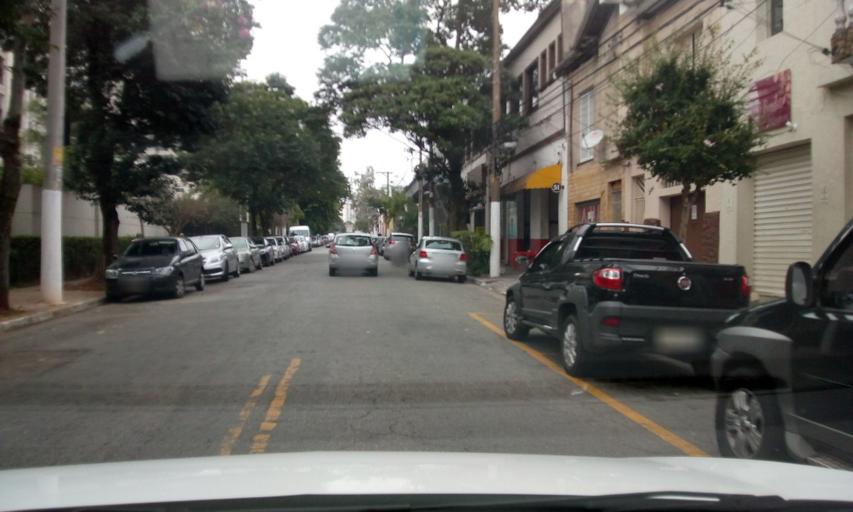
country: BR
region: Sao Paulo
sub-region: Sao Paulo
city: Sao Paulo
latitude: -23.5521
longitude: -46.5958
